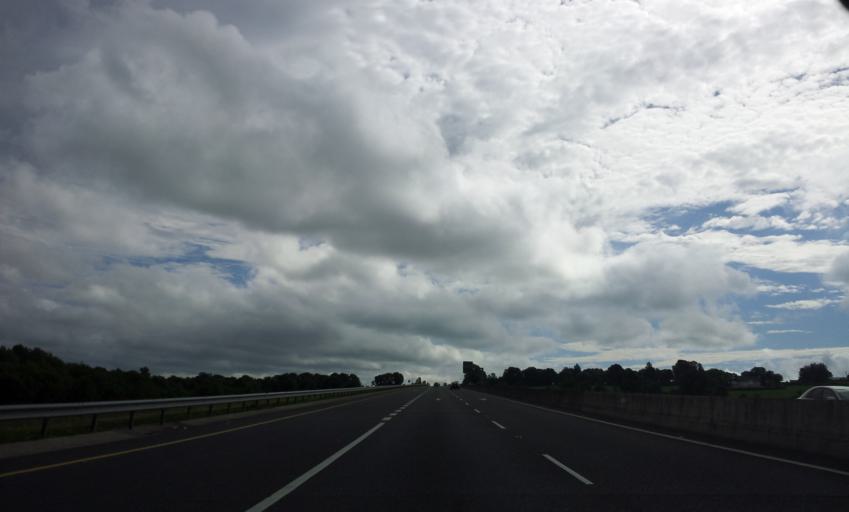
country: IE
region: Munster
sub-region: North Tipperary
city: Nenagh
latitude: 52.8450
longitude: -8.2419
